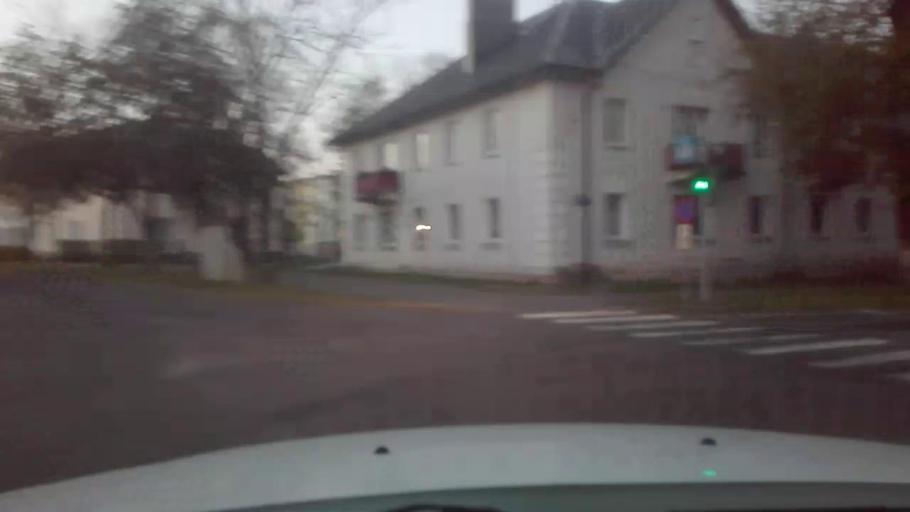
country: EE
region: Harju
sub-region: Maardu linn
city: Maardu
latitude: 59.4798
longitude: 25.0180
